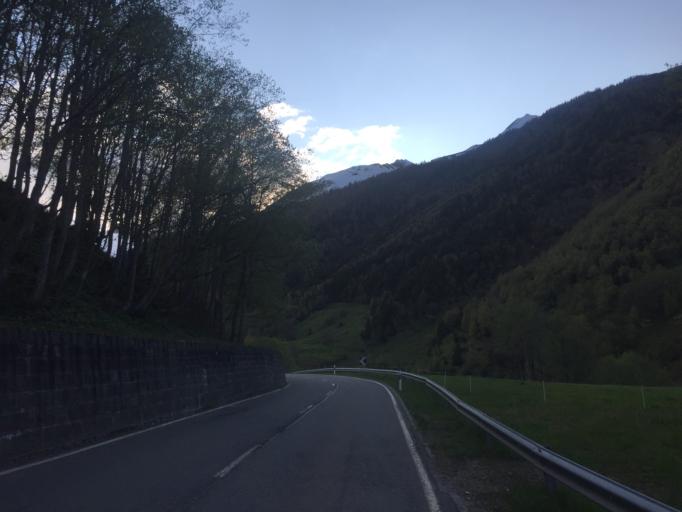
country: CH
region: Ticino
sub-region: Leventina District
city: Airolo
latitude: 46.5193
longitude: 8.5643
